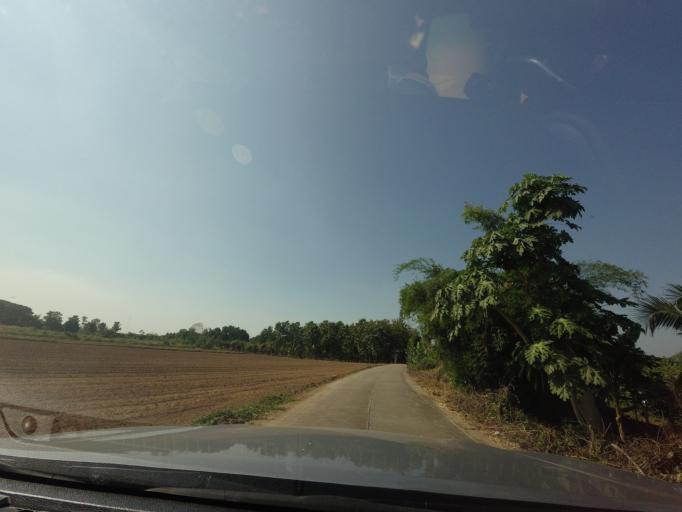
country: TH
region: Sukhothai
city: Sawankhalok
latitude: 17.3229
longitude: 99.8235
